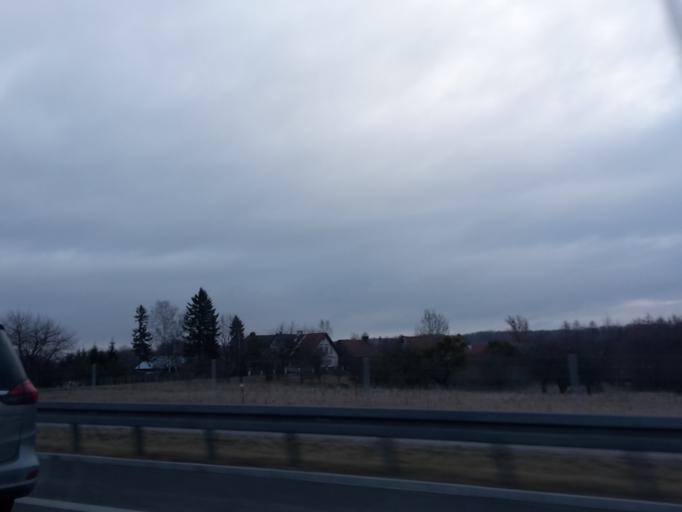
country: PL
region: Warmian-Masurian Voivodeship
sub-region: Powiat ostrodzki
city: Maldyty
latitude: 53.9763
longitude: 19.6971
